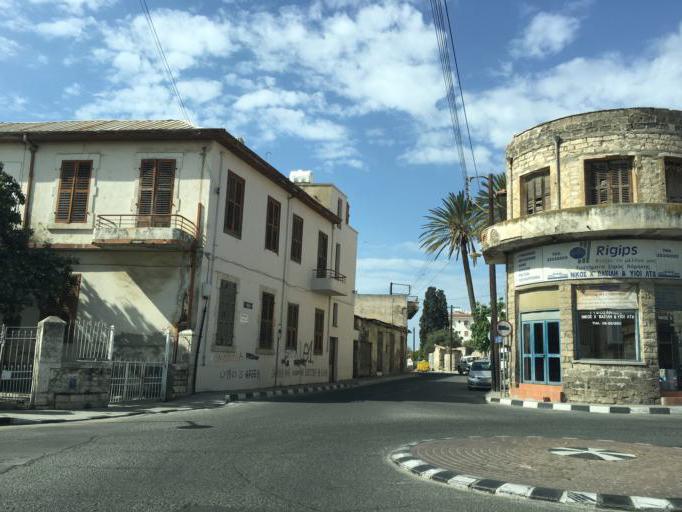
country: CY
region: Limassol
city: Limassol
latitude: 34.6752
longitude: 33.0373
